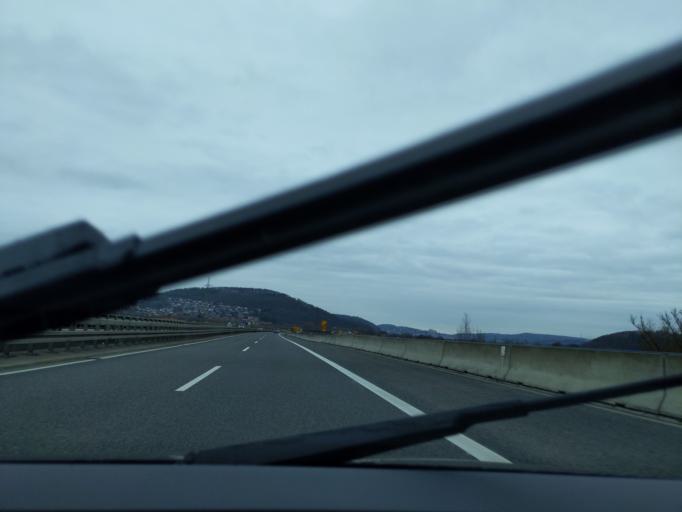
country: DE
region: Hesse
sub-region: Regierungsbezirk Giessen
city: Fronhausen
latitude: 50.7465
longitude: 8.7405
